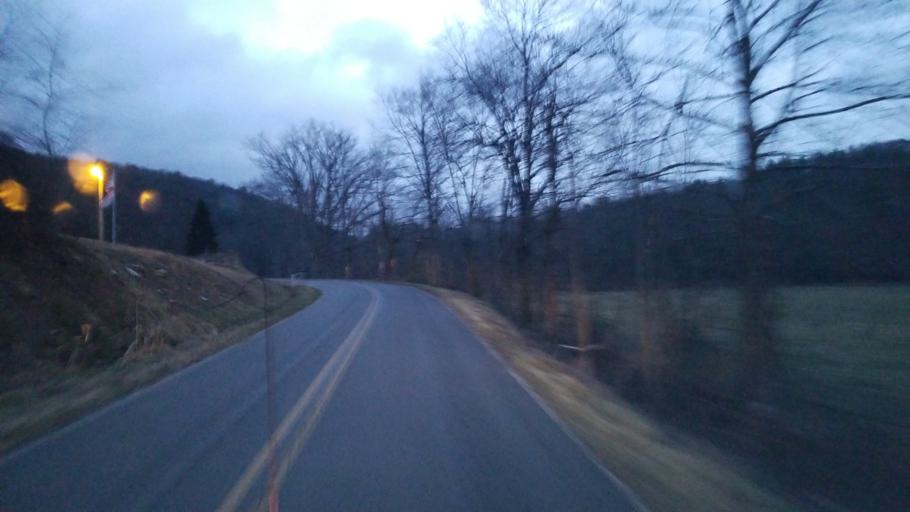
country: US
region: Virginia
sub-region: Pulaski County
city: Pulaski
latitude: 37.1441
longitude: -80.8353
